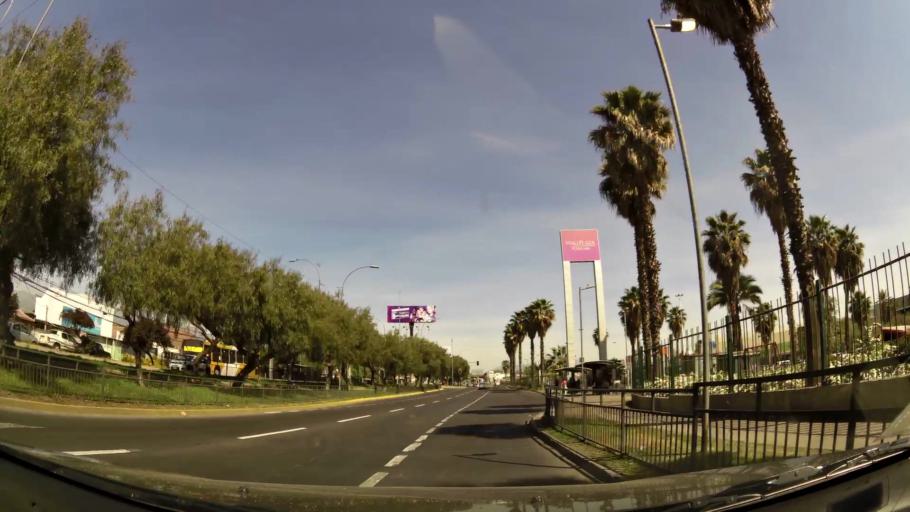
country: CL
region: Santiago Metropolitan
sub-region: Provincia de Cordillera
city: Puente Alto
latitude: -33.5686
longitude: -70.5547
